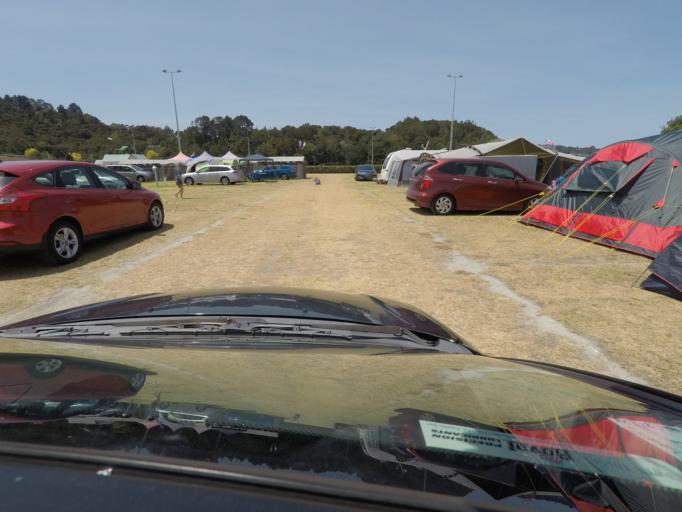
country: NZ
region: Auckland
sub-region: Auckland
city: Warkworth
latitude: -36.3150
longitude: 174.7662
